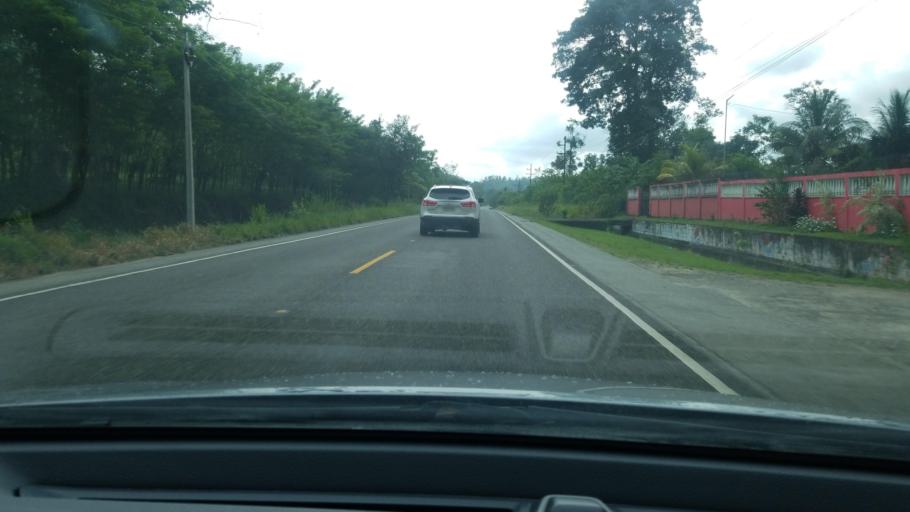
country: HN
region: Cortes
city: Potrerillos
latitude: 15.6157
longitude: -88.2763
